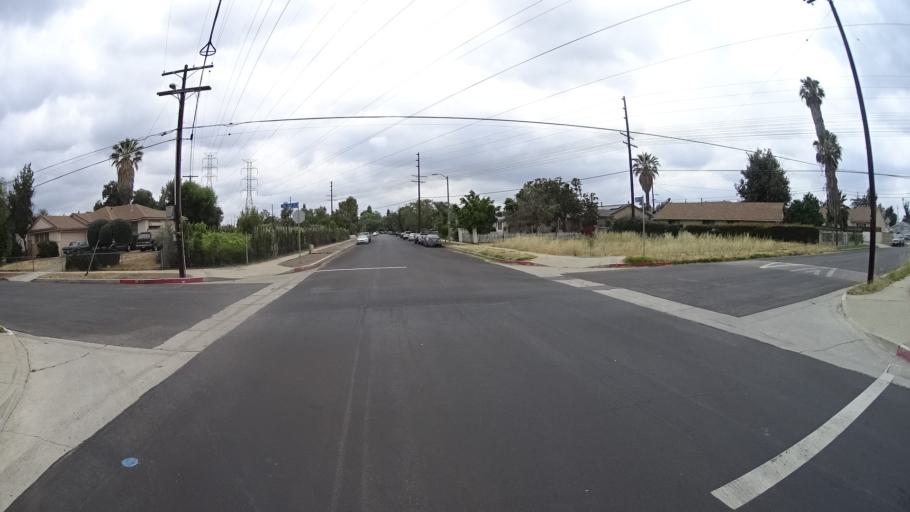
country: US
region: California
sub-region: Los Angeles County
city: San Fernando
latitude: 34.2610
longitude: -118.4531
